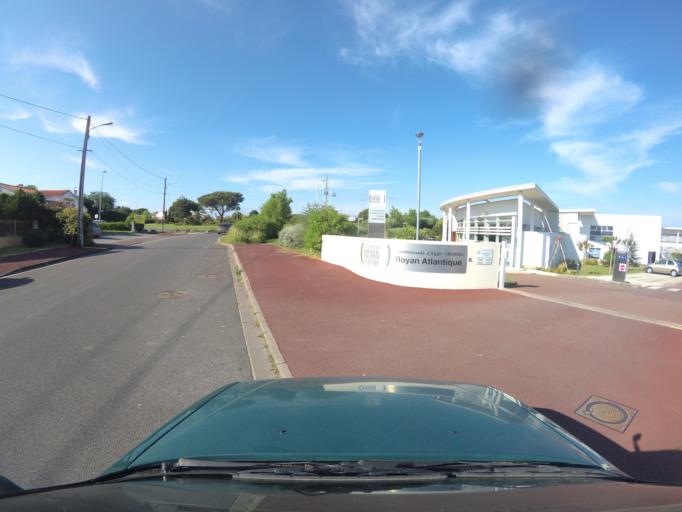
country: FR
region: Poitou-Charentes
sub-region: Departement de la Charente-Maritime
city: Royan
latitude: 45.6384
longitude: -1.0254
